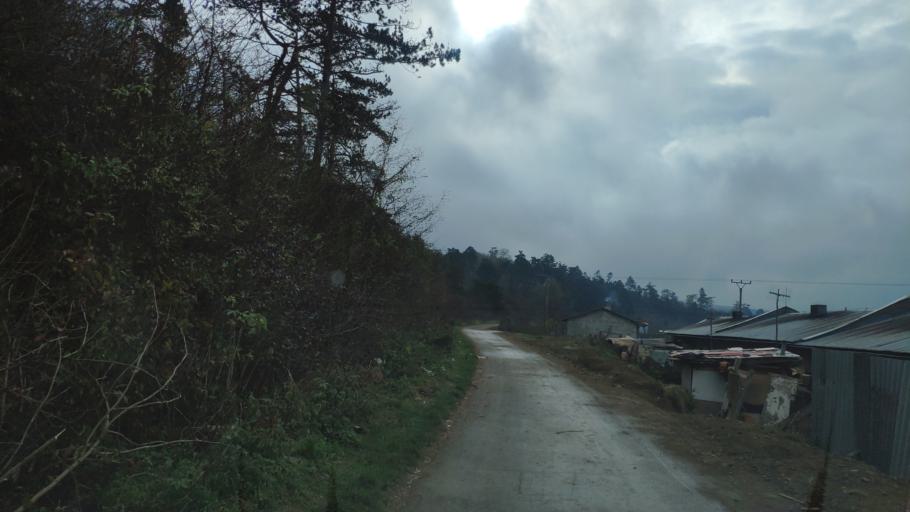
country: SK
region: Presovsky
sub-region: Okres Presov
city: Presov
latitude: 49.0291
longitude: 21.1994
